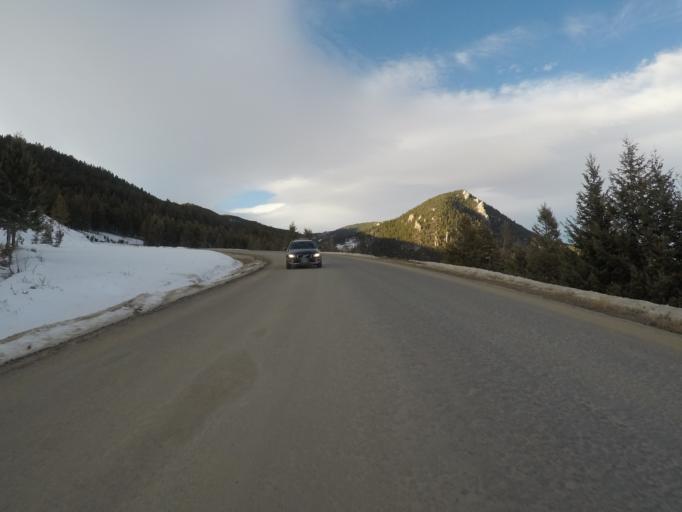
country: US
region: Montana
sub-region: Carbon County
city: Red Lodge
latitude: 45.1656
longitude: -109.3050
